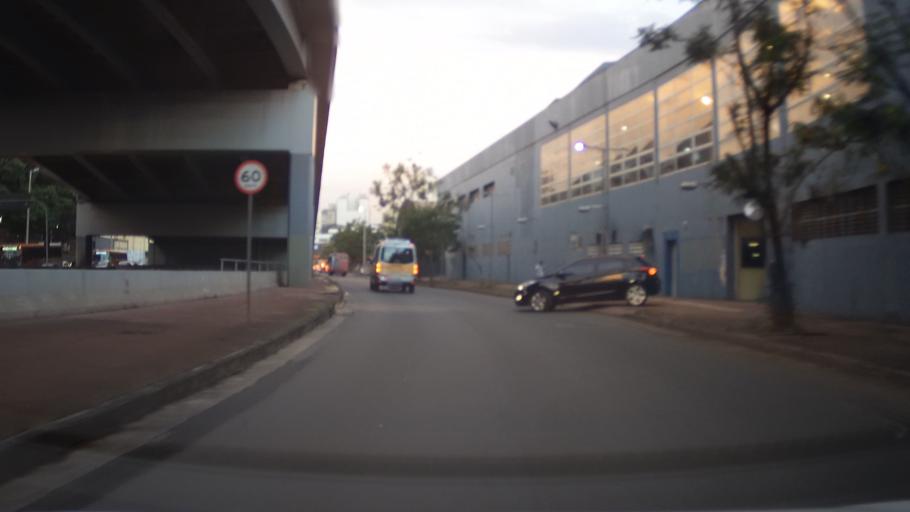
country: BR
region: Minas Gerais
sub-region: Belo Horizonte
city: Belo Horizonte
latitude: -19.9188
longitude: -43.9606
